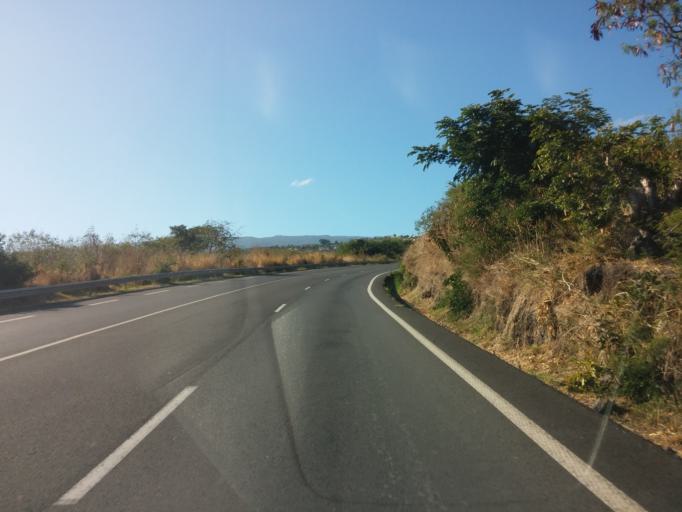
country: RE
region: Reunion
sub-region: Reunion
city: Saint-Paul
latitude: -21.0205
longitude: 55.2722
